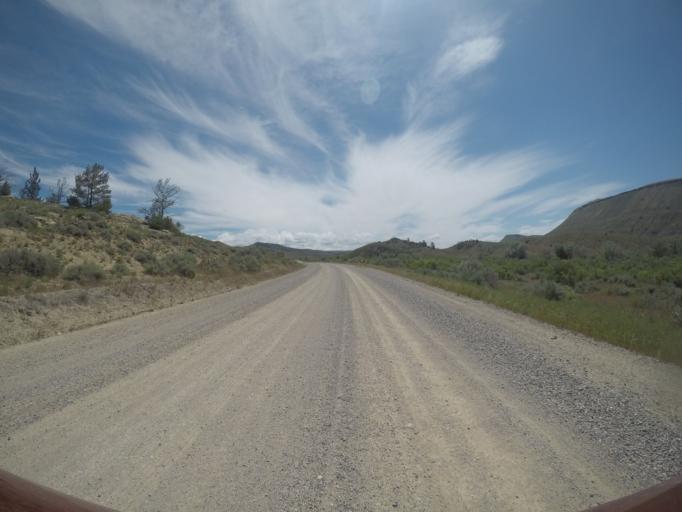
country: US
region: Montana
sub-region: Carbon County
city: Red Lodge
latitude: 45.2102
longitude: -108.8371
